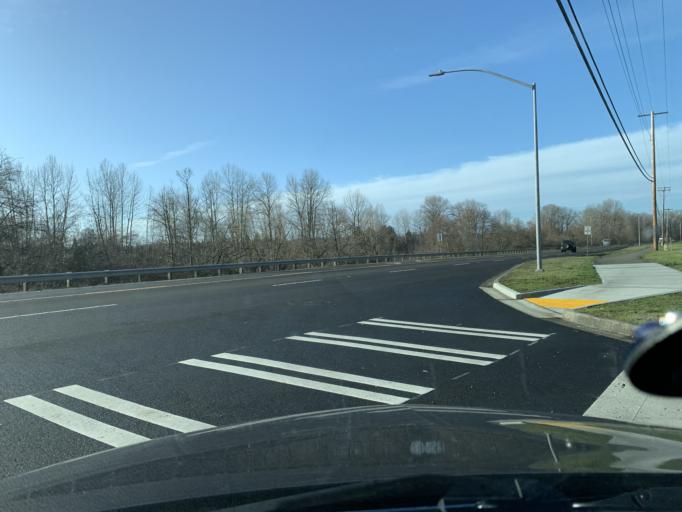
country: US
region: Washington
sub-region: Pierce County
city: North Puyallup
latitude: 47.2039
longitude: -122.2989
